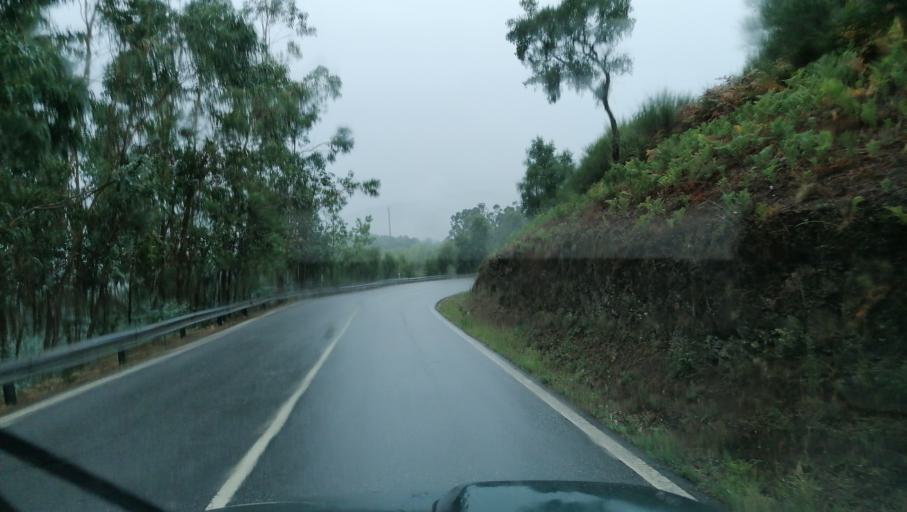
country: PT
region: Braga
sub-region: Cabeceiras de Basto
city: Cabeceiras de Basto
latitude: 41.4899
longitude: -7.9352
